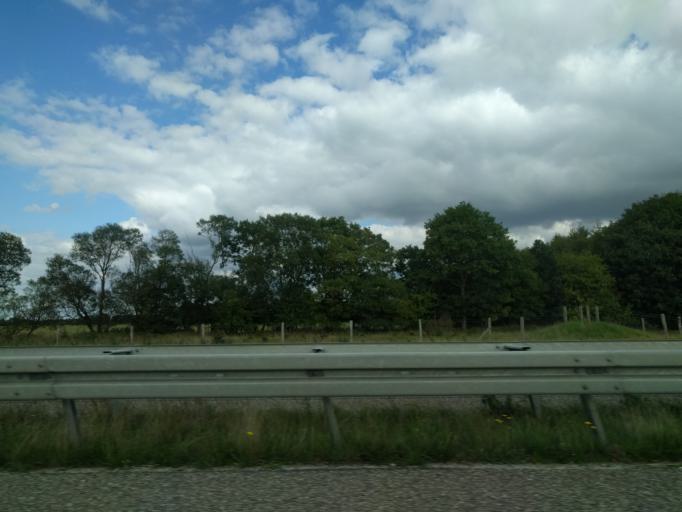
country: DK
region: South Denmark
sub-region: Vejle Kommune
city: Give
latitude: 55.9016
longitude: 9.2096
